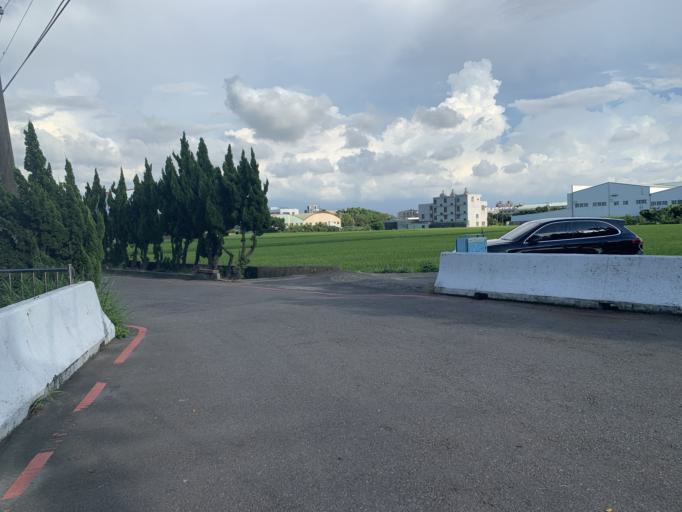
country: TW
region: Taiwan
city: Fengyuan
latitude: 24.2379
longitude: 120.6528
